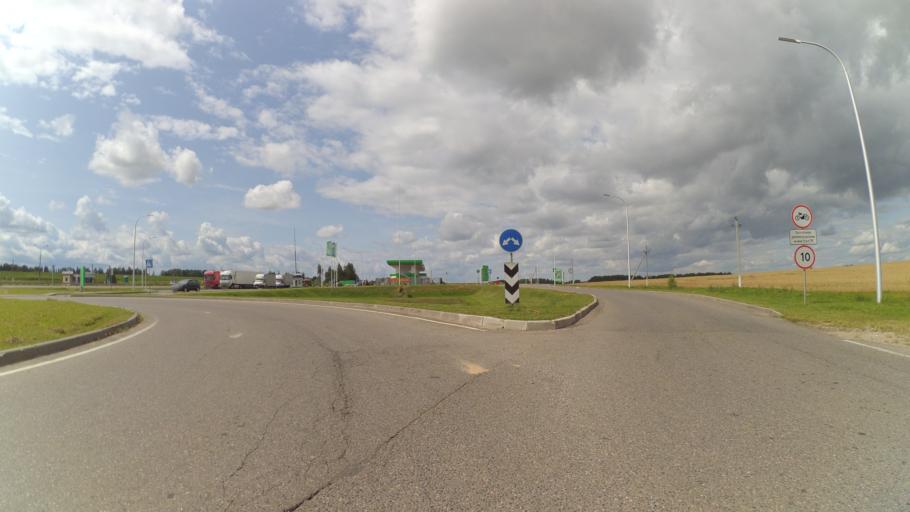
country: BY
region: Minsk
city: Ivyanyets
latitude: 54.0524
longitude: 26.7725
